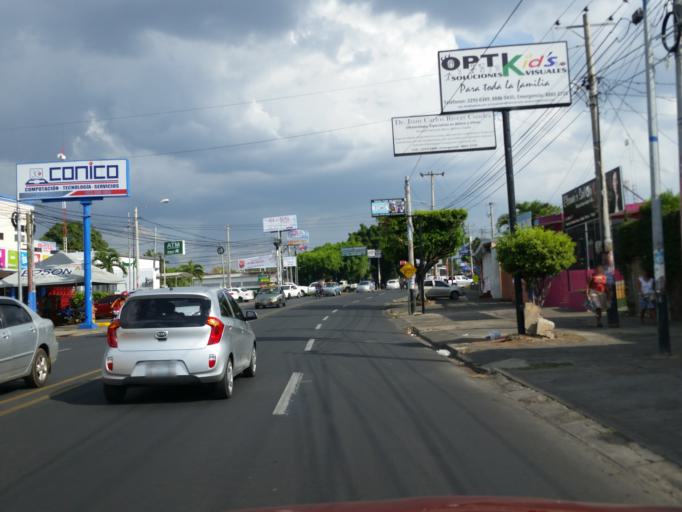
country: NI
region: Managua
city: Managua
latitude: 12.1222
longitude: -86.2527
